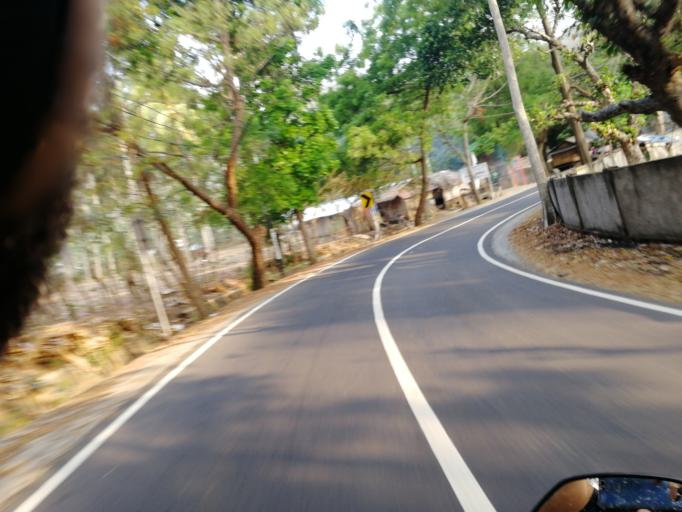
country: ID
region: West Nusa Tenggara
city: Karangsubagan
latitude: -8.4656
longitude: 116.0381
